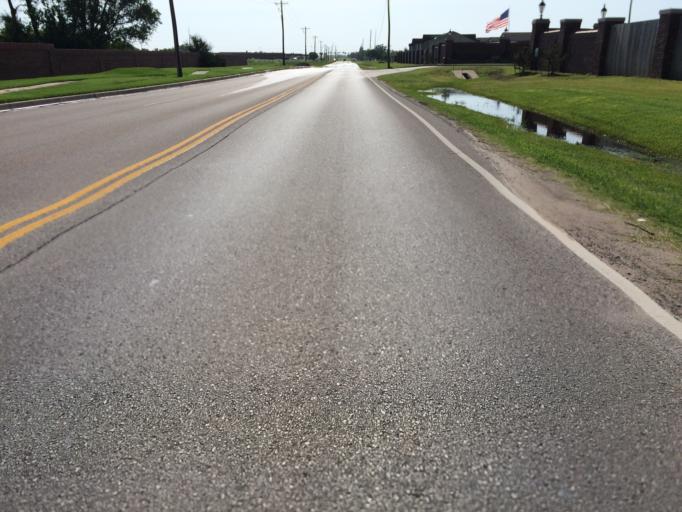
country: US
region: Oklahoma
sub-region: Cleveland County
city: Norman
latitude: 35.2474
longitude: -97.4997
